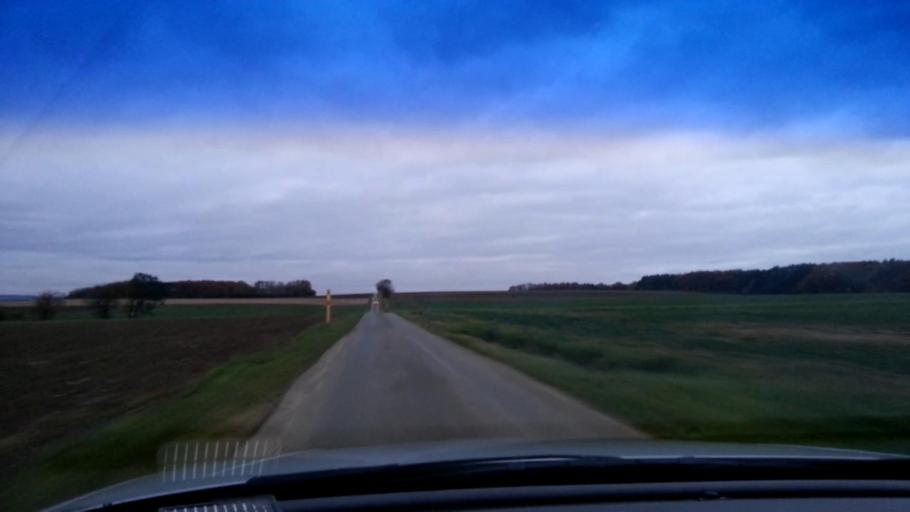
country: DE
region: Bavaria
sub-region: Upper Franconia
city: Memmelsdorf
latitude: 49.9571
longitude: 10.9475
